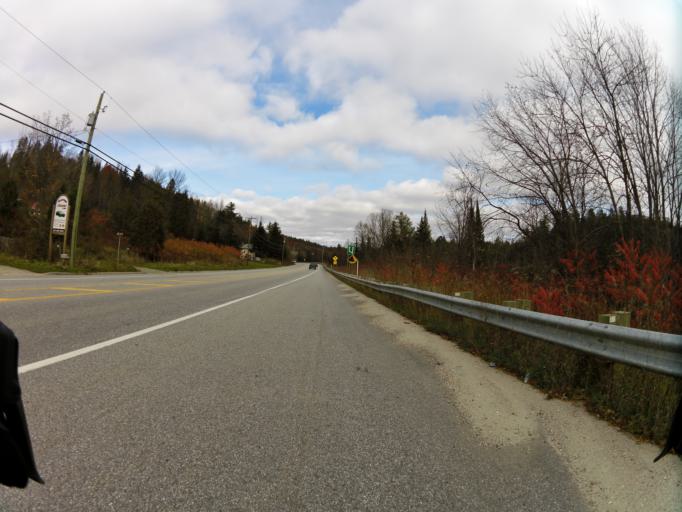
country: CA
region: Quebec
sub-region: Outaouais
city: Wakefield
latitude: 45.6589
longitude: -75.9279
